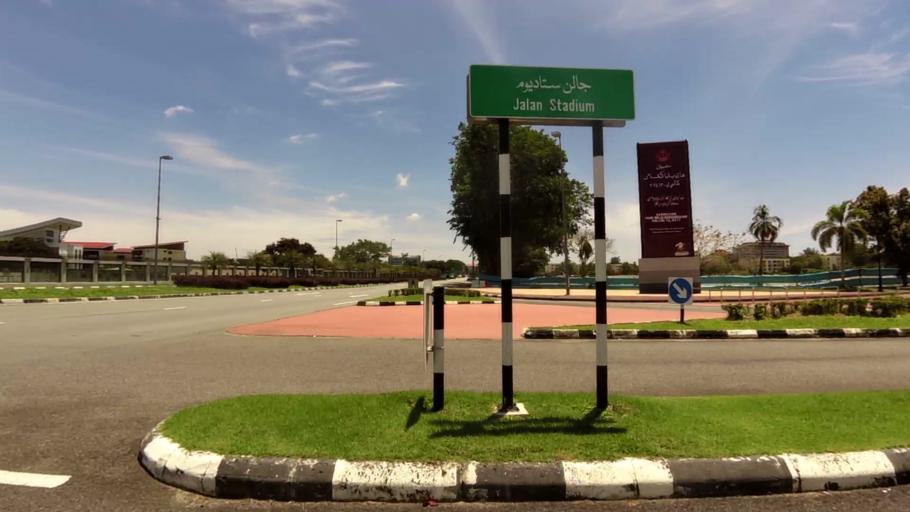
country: BN
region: Brunei and Muara
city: Bandar Seri Begawan
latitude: 4.9290
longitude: 114.9394
